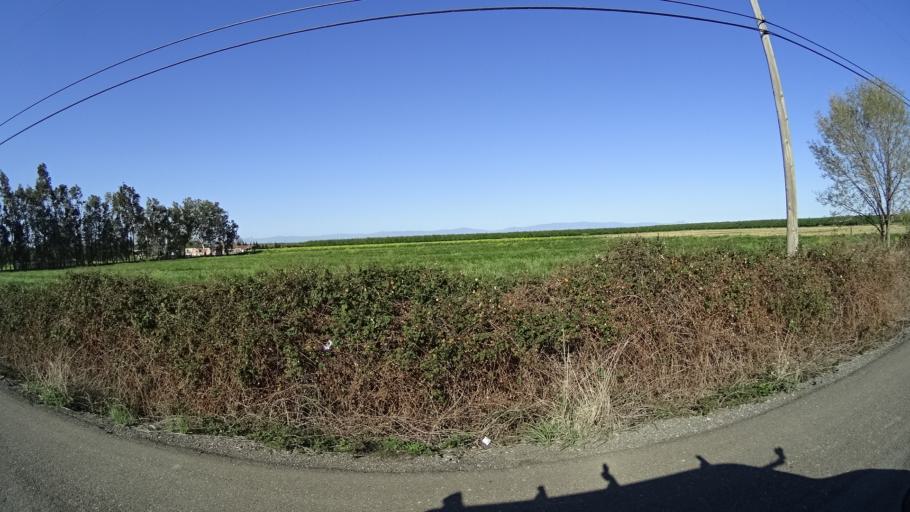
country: US
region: California
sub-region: Glenn County
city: Orland
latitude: 39.8054
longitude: -122.1041
